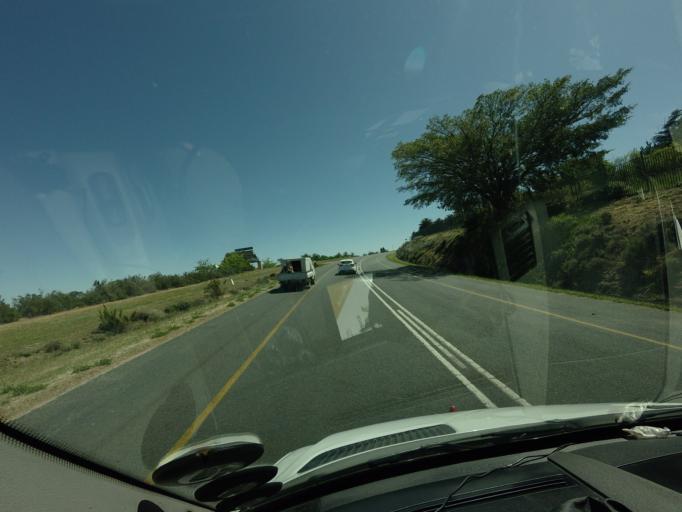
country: ZA
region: Western Cape
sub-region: Cape Winelands District Municipality
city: Stellenbosch
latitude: -33.8836
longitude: 18.8475
